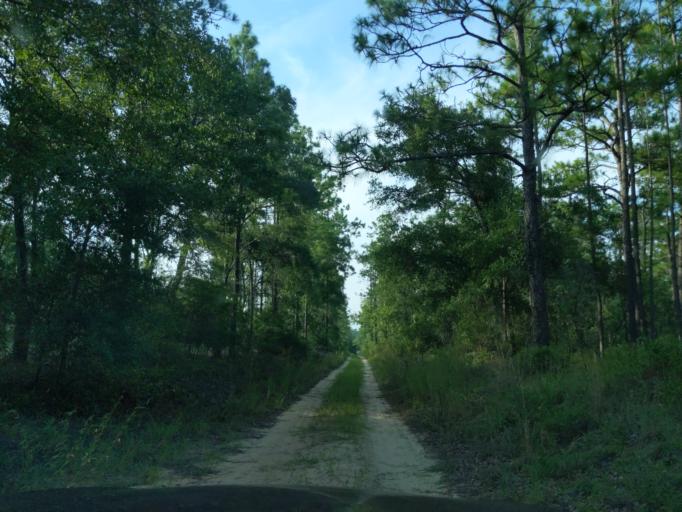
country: US
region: Florida
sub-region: Leon County
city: Tallahassee
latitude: 30.3616
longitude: -84.3611
